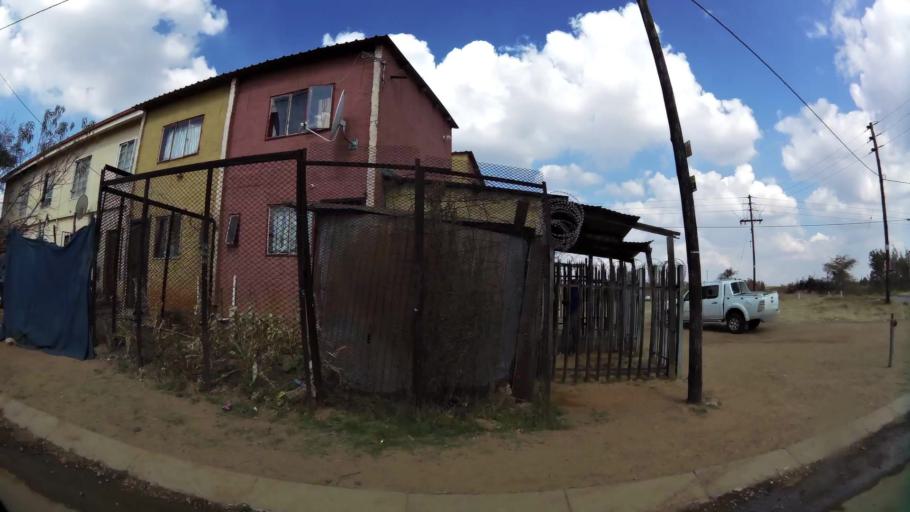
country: ZA
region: Gauteng
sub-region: City of Johannesburg Metropolitan Municipality
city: Roodepoort
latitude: -26.1847
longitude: 27.8422
